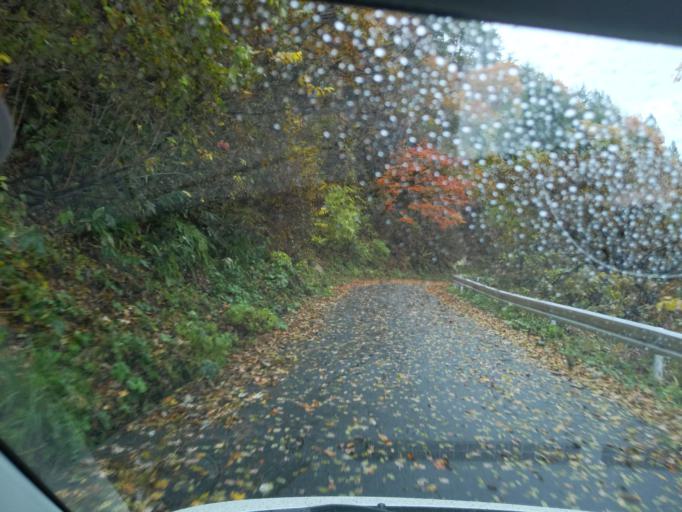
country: JP
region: Iwate
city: Mizusawa
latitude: 39.1020
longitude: 140.9402
